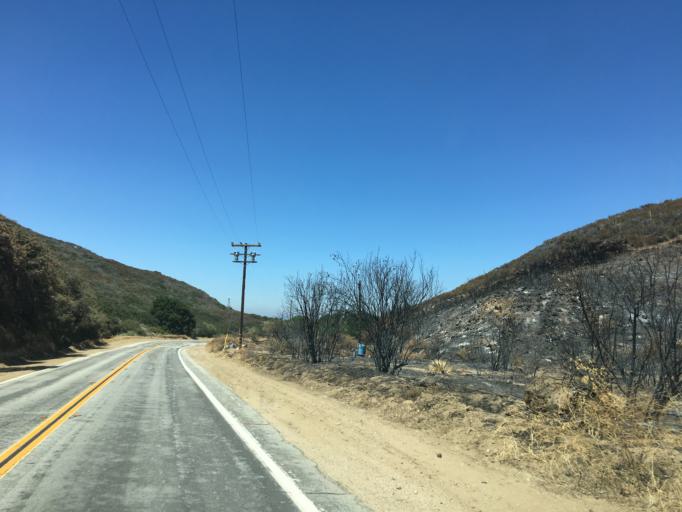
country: US
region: California
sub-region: Los Angeles County
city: Leona Valley
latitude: 34.5828
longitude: -118.3357
